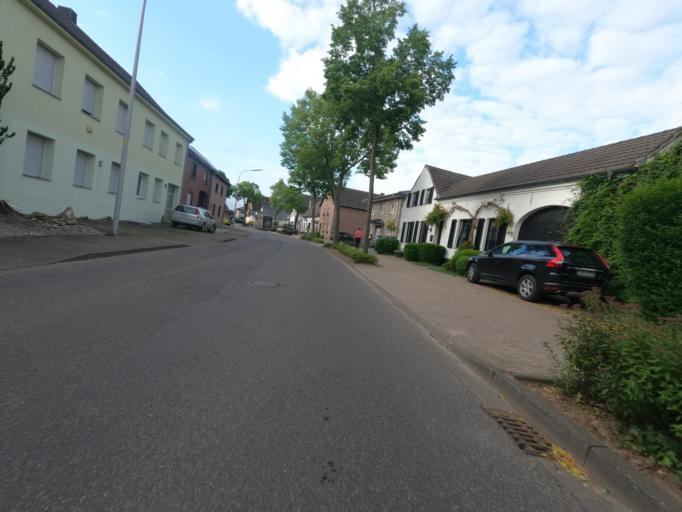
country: DE
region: North Rhine-Westphalia
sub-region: Regierungsbezirk Koln
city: Heinsberg
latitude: 51.0928
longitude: 6.1016
